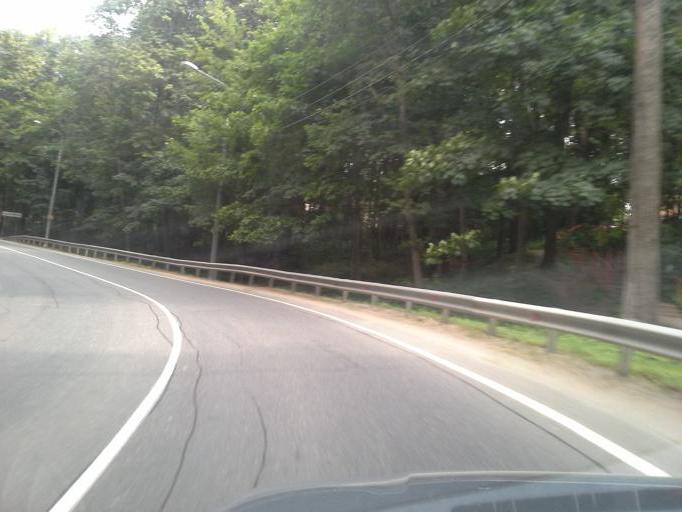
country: RU
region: Moskovskaya
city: Barvikha
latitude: 55.7272
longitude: 37.2759
